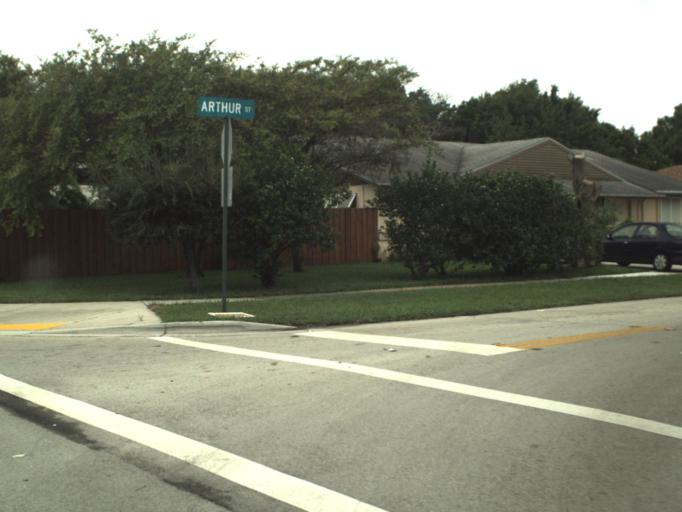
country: US
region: Florida
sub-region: Palm Beach County
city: North Palm Beach
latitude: 26.8132
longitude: -80.1063
